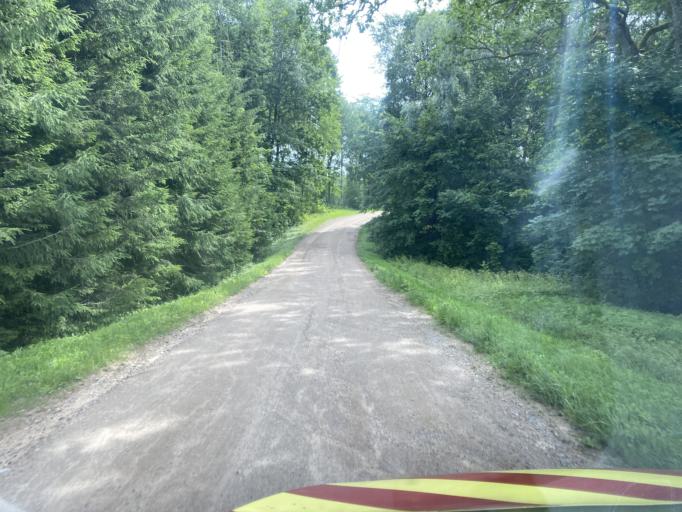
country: EE
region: Viljandimaa
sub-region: Karksi vald
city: Karksi-Nuia
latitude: 58.0957
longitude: 25.4699
